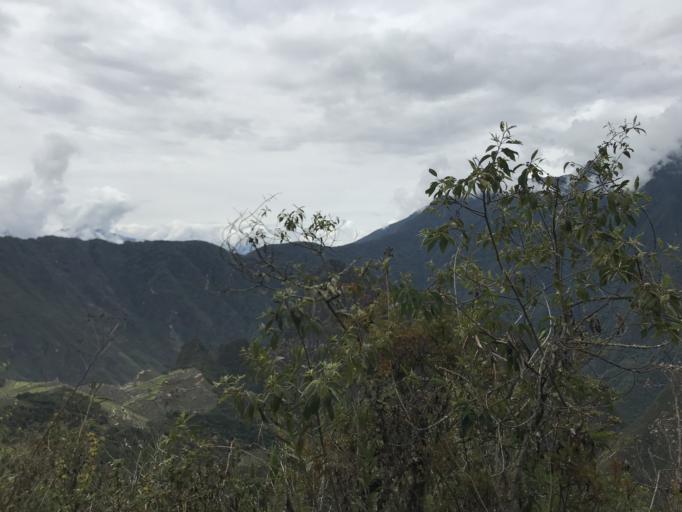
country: PE
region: Cusco
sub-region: Provincia de La Convencion
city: Santa Teresa
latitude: -13.1697
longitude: -72.5356
